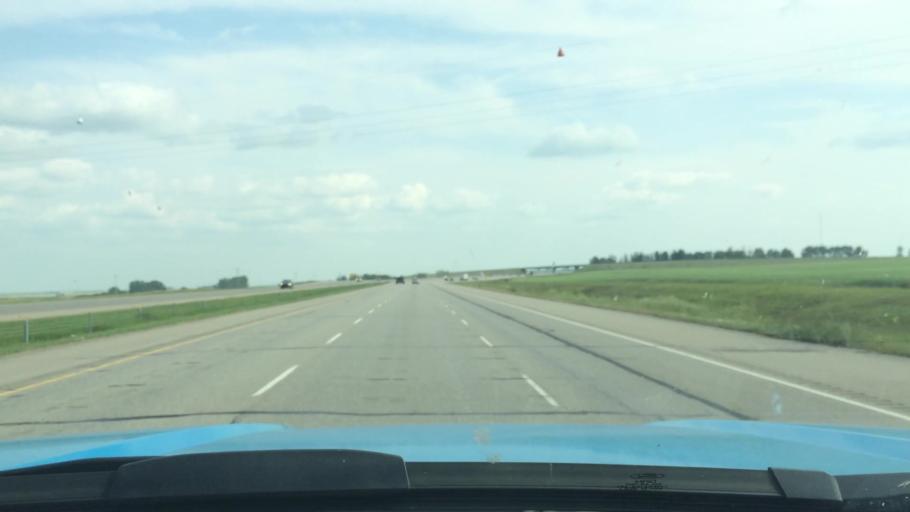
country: CA
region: Alberta
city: Crossfield
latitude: 51.4387
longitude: -114.0057
